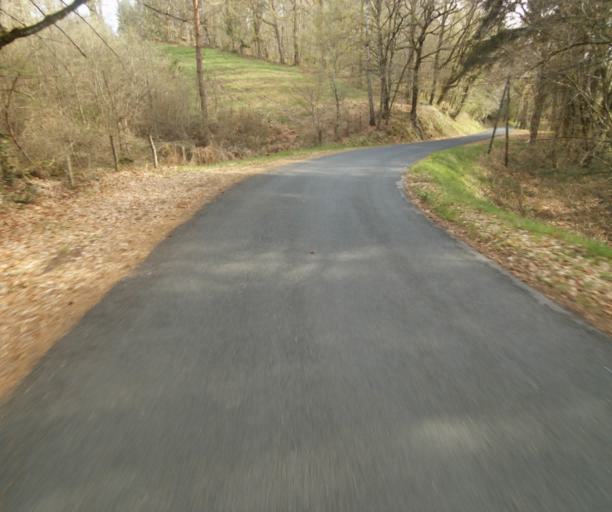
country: FR
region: Limousin
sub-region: Departement de la Correze
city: Correze
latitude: 45.3620
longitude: 1.8575
